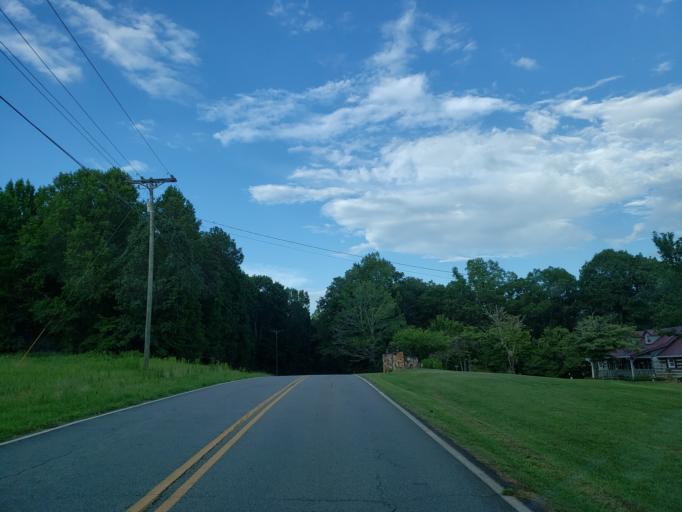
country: US
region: Georgia
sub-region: Cherokee County
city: Canton
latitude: 34.3302
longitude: -84.5029
